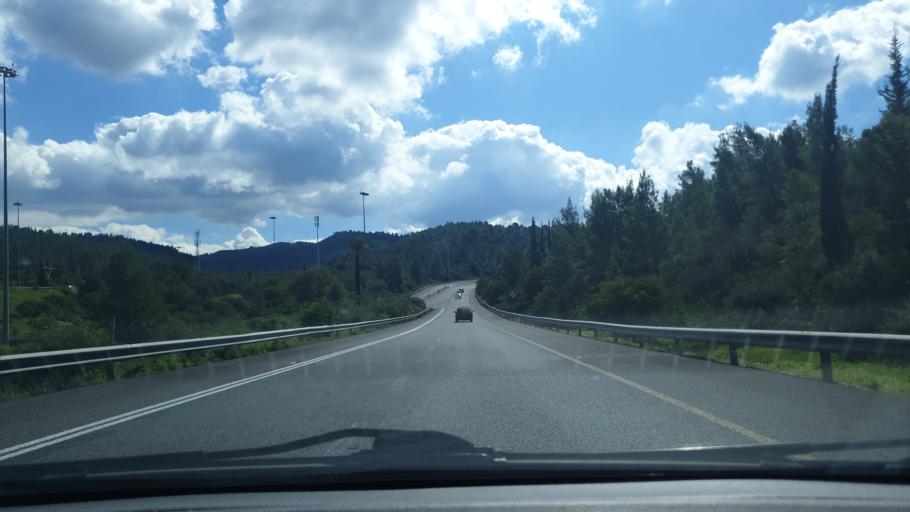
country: IL
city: Mevo horon
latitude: 31.8183
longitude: 35.0202
